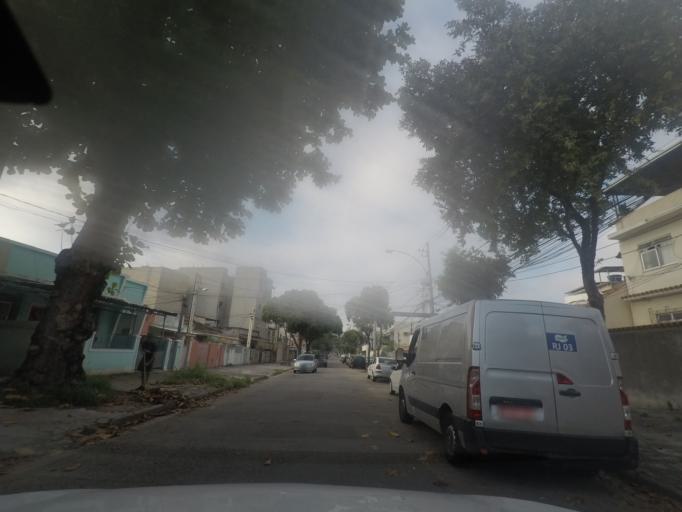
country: BR
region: Rio de Janeiro
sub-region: Duque De Caxias
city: Duque de Caxias
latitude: -22.8333
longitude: -43.2729
